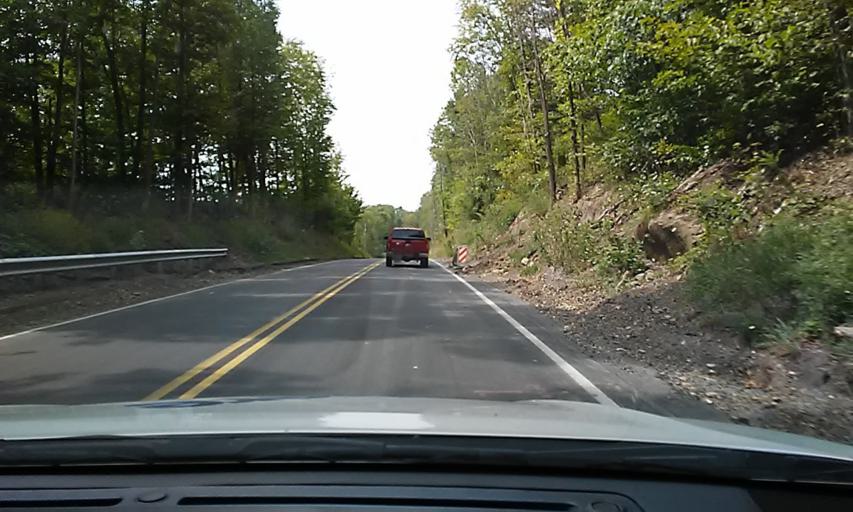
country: US
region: Pennsylvania
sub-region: Clearfield County
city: Treasure Lake
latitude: 41.1838
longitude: -78.6329
